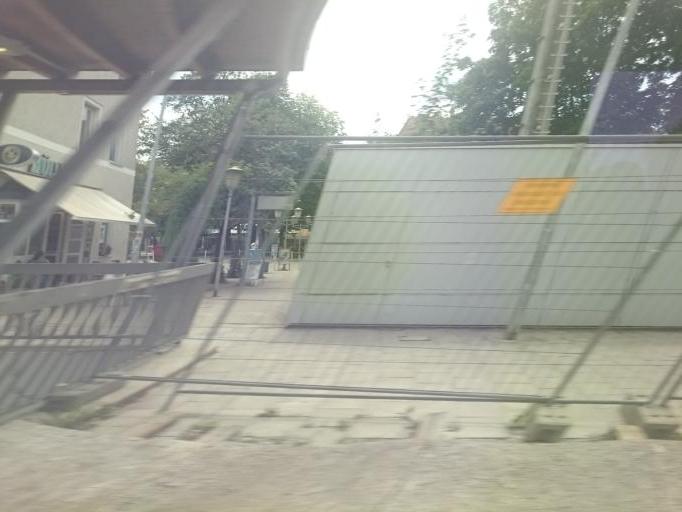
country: DE
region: Bavaria
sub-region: Upper Bavaria
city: Haar
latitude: 48.1112
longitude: 11.7308
